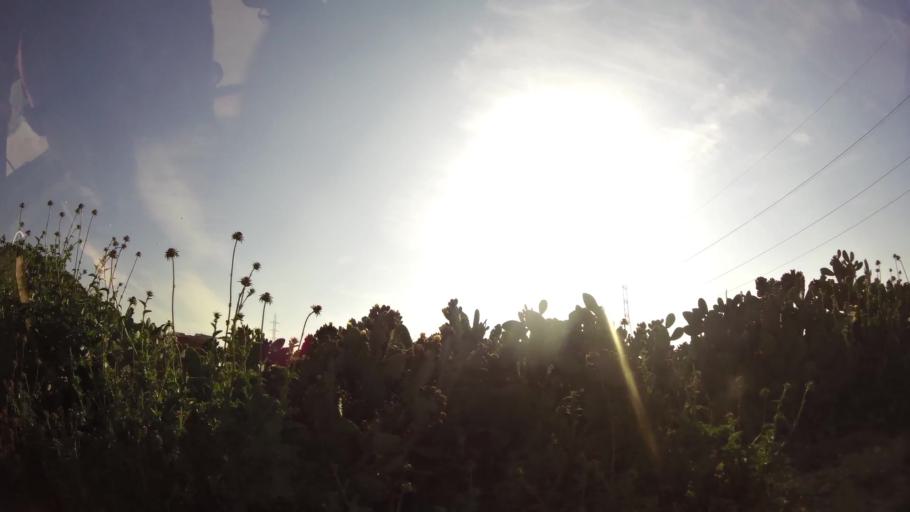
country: MA
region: Oriental
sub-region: Oujda-Angad
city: Oujda
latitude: 34.7185
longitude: -1.9052
